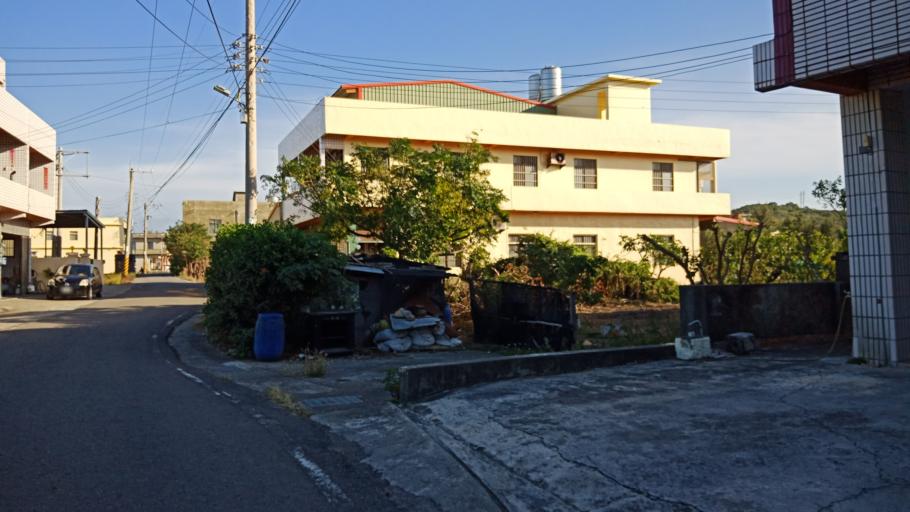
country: TW
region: Taiwan
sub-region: Miaoli
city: Miaoli
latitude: 24.4901
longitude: 120.6925
